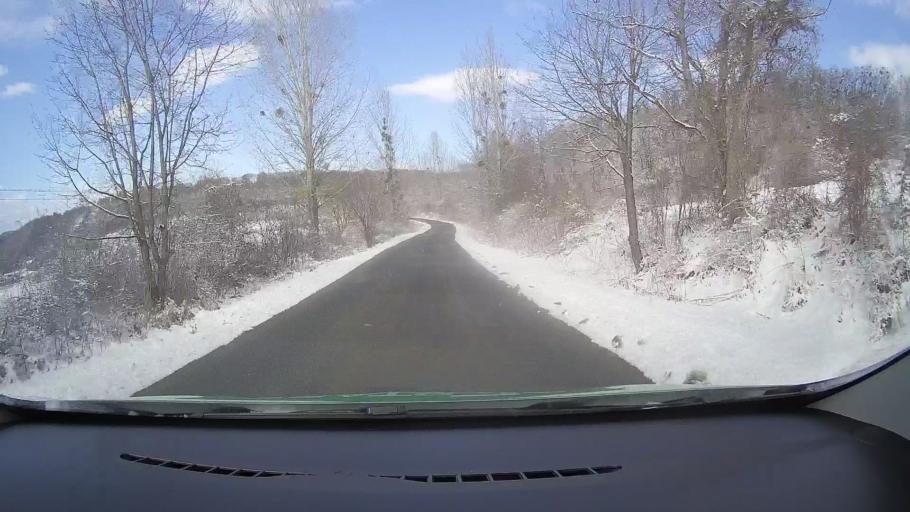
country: RO
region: Sibiu
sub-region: Comuna Mosna
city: Mosna
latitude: 46.0107
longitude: 24.4222
